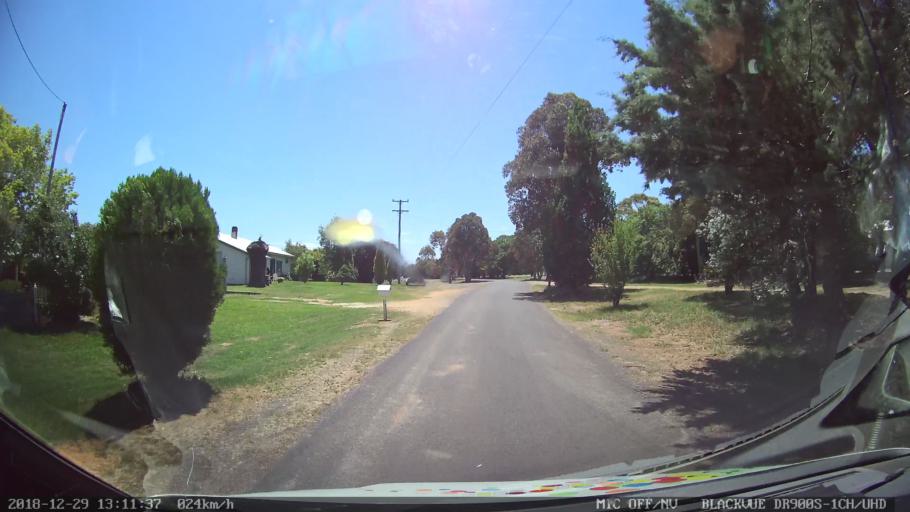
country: AU
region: Australian Capital Territory
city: Macarthur
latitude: -35.7124
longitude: 149.1653
